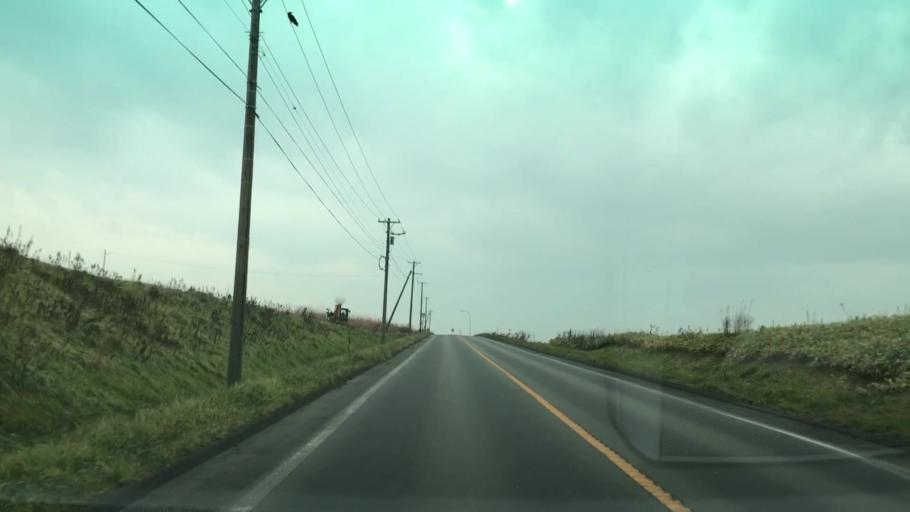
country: JP
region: Hokkaido
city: Ishikari
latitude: 43.3522
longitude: 141.4269
